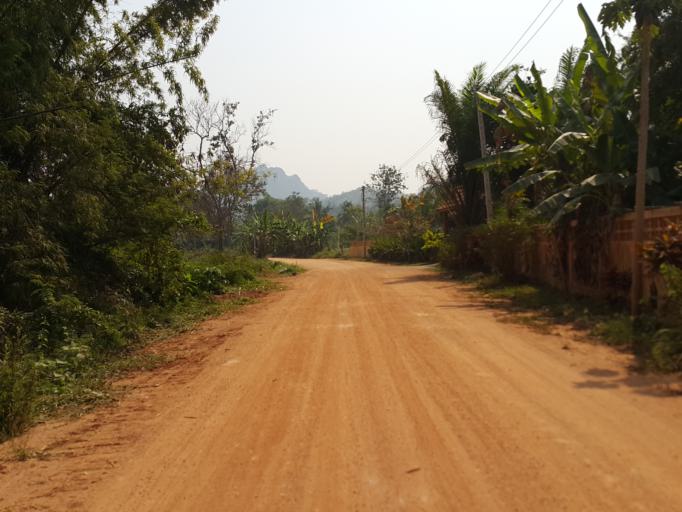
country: TH
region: Sukhothai
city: Thung Saliam
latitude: 17.3311
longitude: 99.4941
